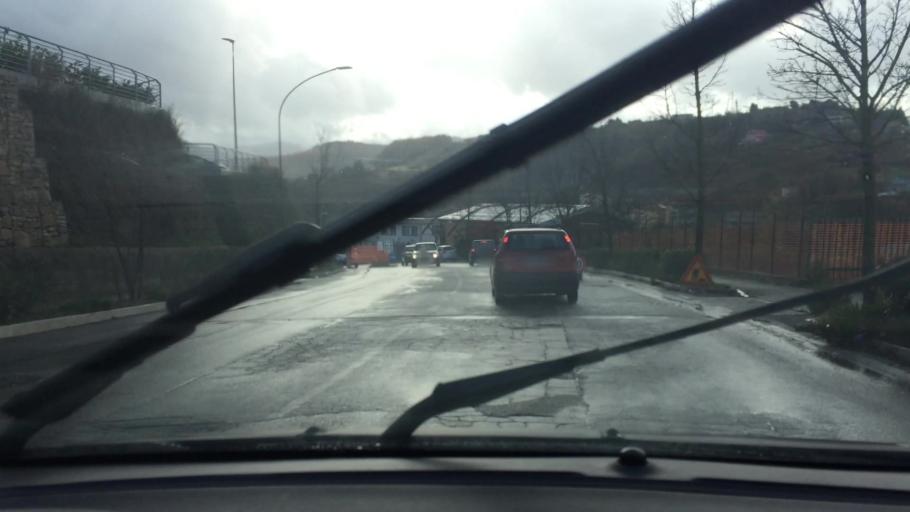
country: IT
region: Basilicate
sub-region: Provincia di Potenza
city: Potenza
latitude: 40.6378
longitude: 15.7868
